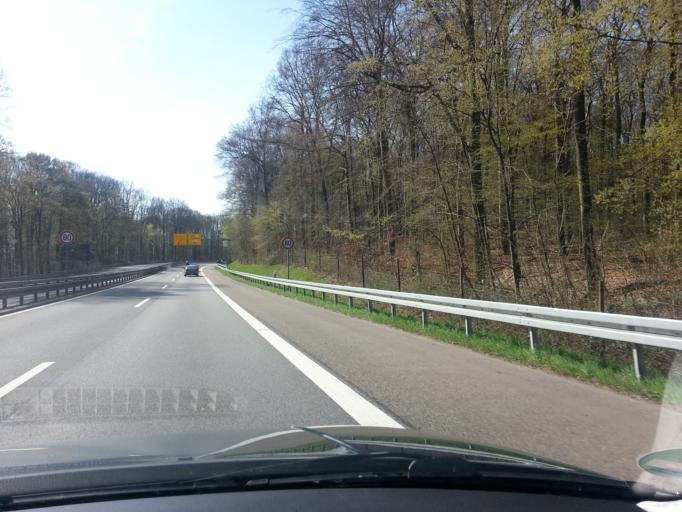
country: DE
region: Saarland
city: Saarbrucken
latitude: 49.2634
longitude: 6.9938
